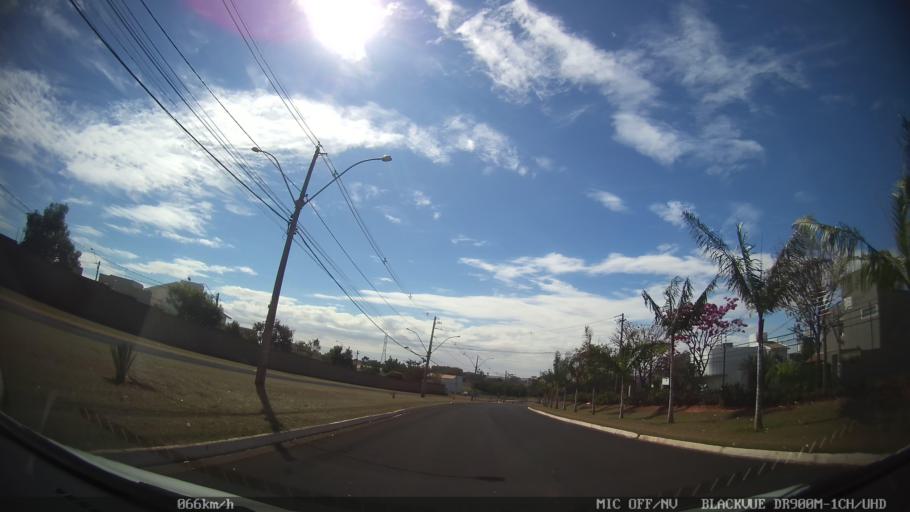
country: BR
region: Sao Paulo
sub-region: Sao Jose Do Rio Preto
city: Sao Jose do Rio Preto
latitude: -20.8197
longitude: -49.4807
